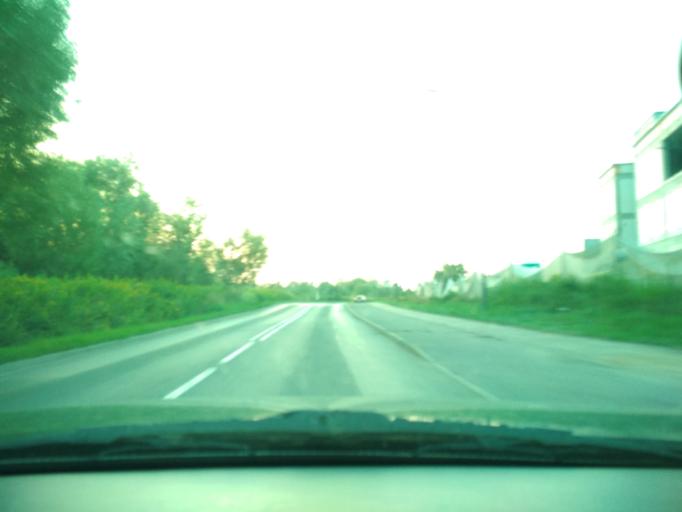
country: PL
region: Silesian Voivodeship
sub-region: Gliwice
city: Gliwice
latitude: 50.2735
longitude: 18.6836
